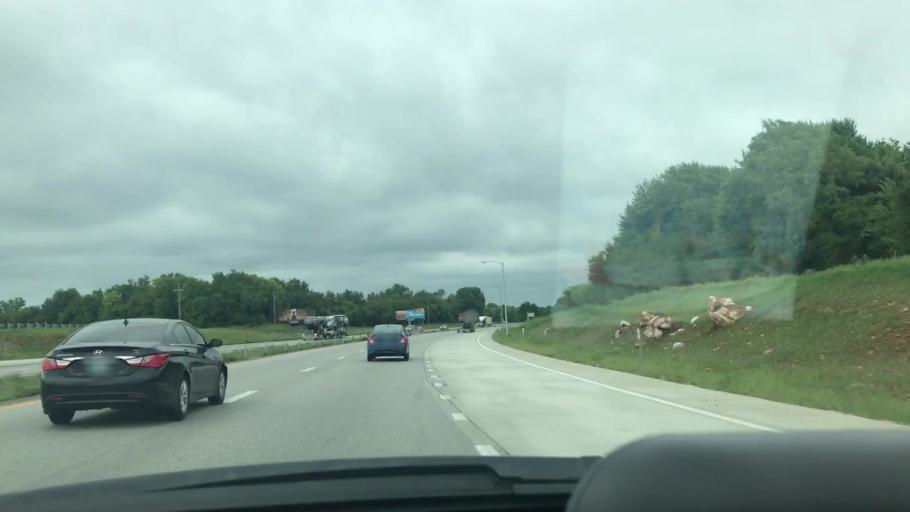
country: US
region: Missouri
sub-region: Greene County
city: Springfield
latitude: 37.2481
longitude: -93.3441
